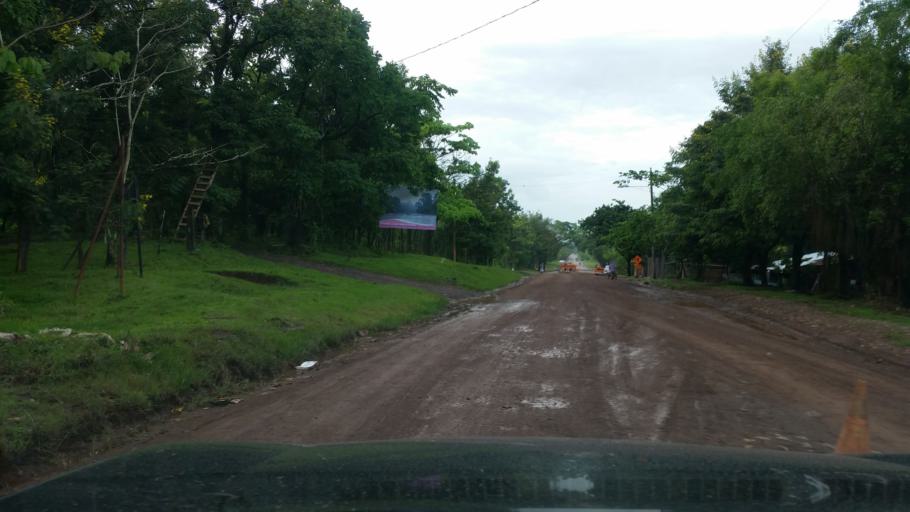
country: NI
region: Matagalpa
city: Rio Blanco
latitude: 13.1850
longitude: -84.9508
